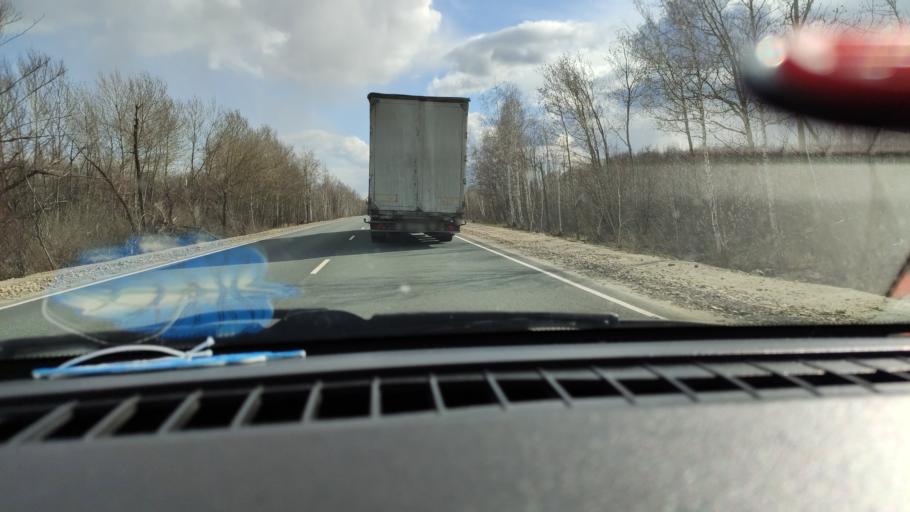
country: RU
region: Saratov
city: Alekseyevka
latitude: 52.4230
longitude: 48.0082
